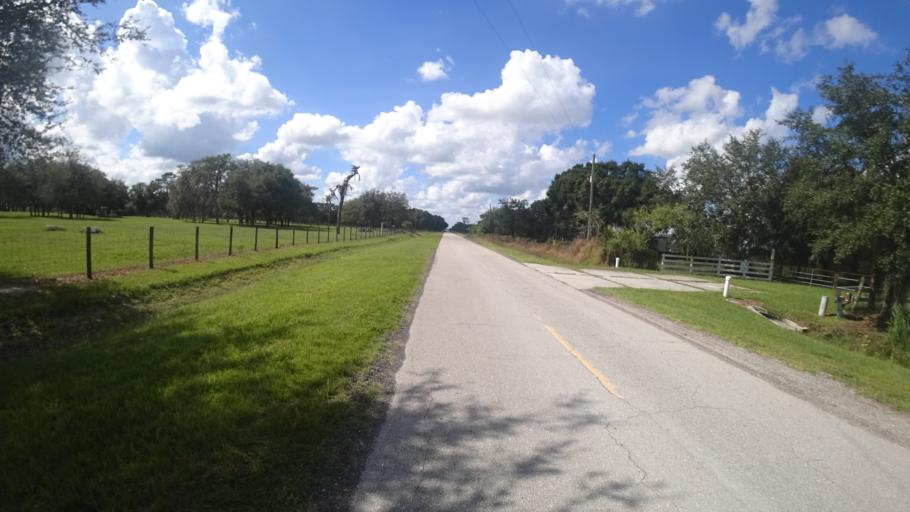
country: US
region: Florida
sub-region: Sarasota County
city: Warm Mineral Springs
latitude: 27.2736
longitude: -82.1546
